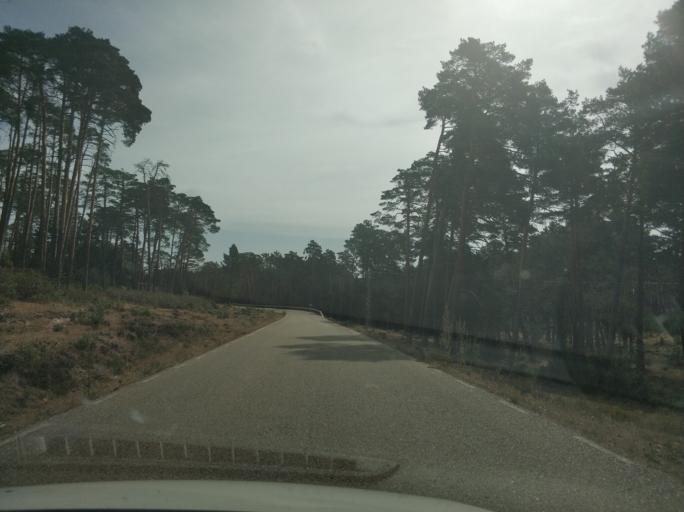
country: ES
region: Castille and Leon
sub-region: Provincia de Soria
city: Navaleno
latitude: 41.8535
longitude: -2.9629
